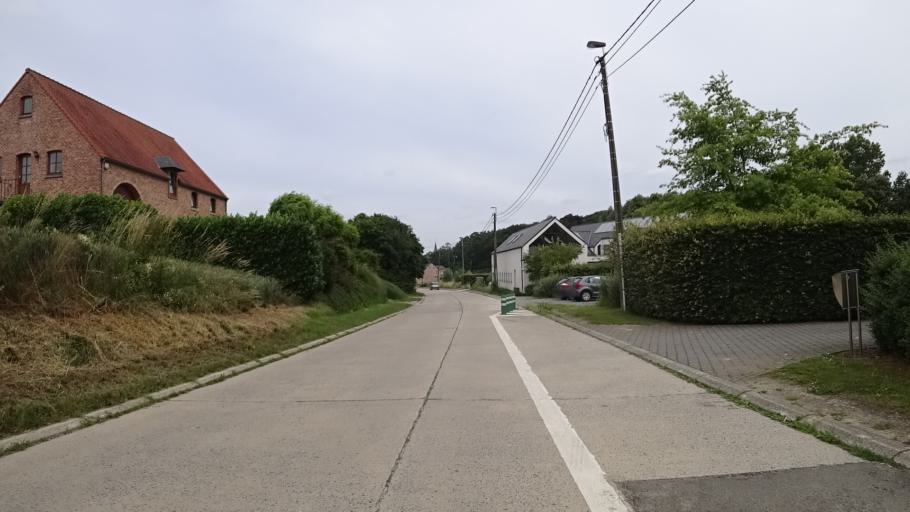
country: BE
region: Wallonia
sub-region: Province du Brabant Wallon
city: Louvain-la-Neuve
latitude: 50.6714
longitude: 4.6503
